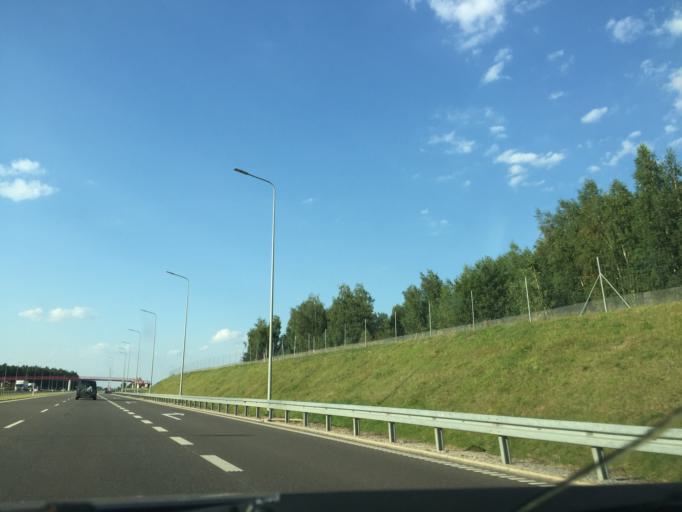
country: PL
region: Masovian Voivodeship
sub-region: Powiat radomski
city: Zakrzew
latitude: 51.4405
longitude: 21.0341
